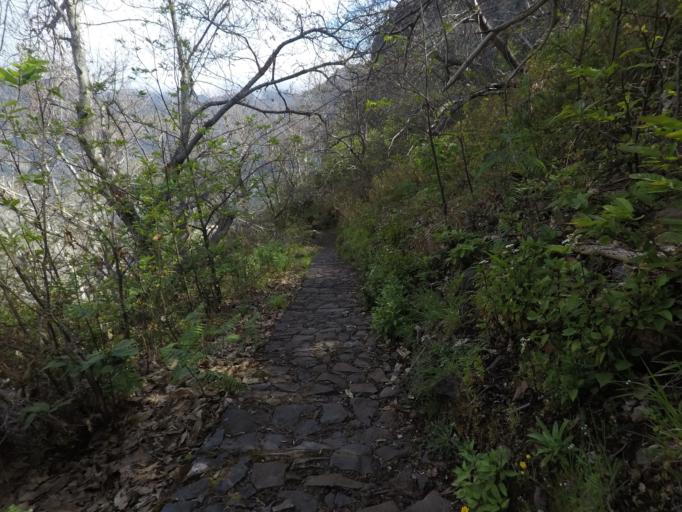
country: PT
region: Madeira
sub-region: Camara de Lobos
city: Curral das Freiras
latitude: 32.7108
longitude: -16.9627
